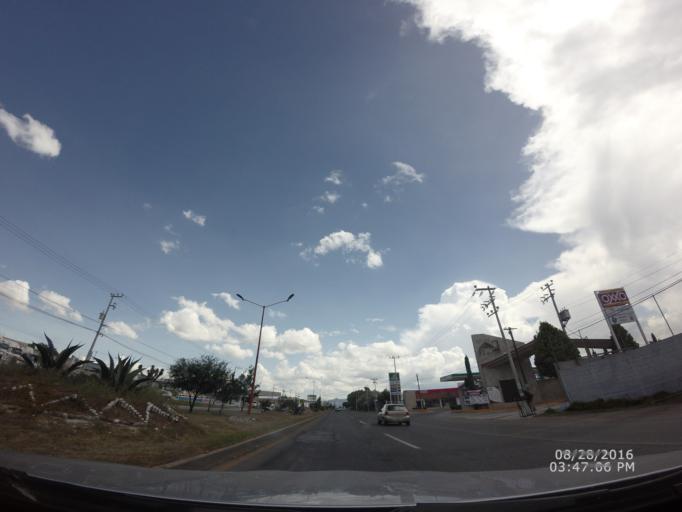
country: MX
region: Hidalgo
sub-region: Mineral de la Reforma
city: Nuevo Centro de Poblacion Agricola el Chacon
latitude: 20.0686
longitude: -98.7445
